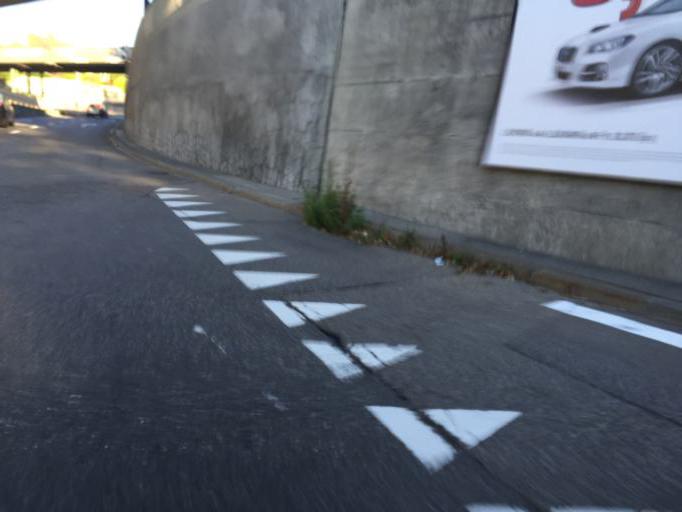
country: CH
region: Bern
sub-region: Bern-Mittelland District
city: Koniz
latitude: 46.9419
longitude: 7.4034
